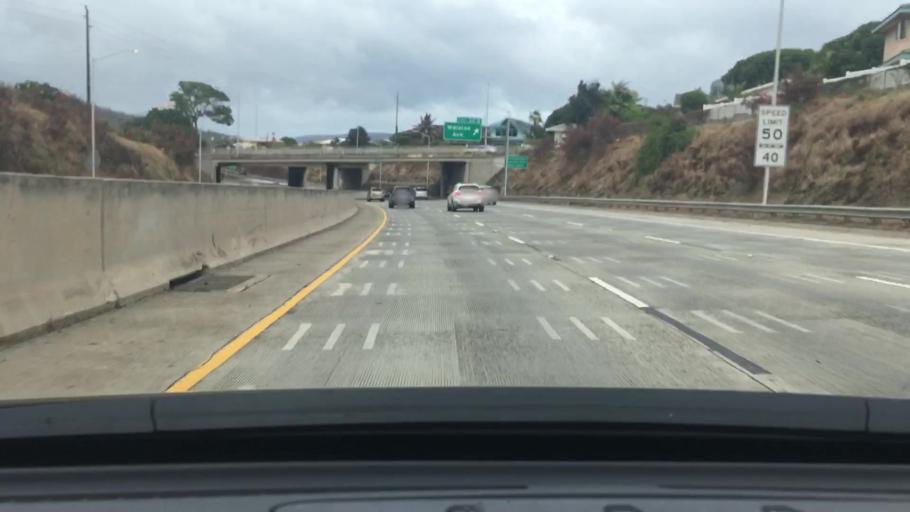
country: US
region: Hawaii
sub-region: Honolulu County
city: Honolulu
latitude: 21.2786
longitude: -157.7964
